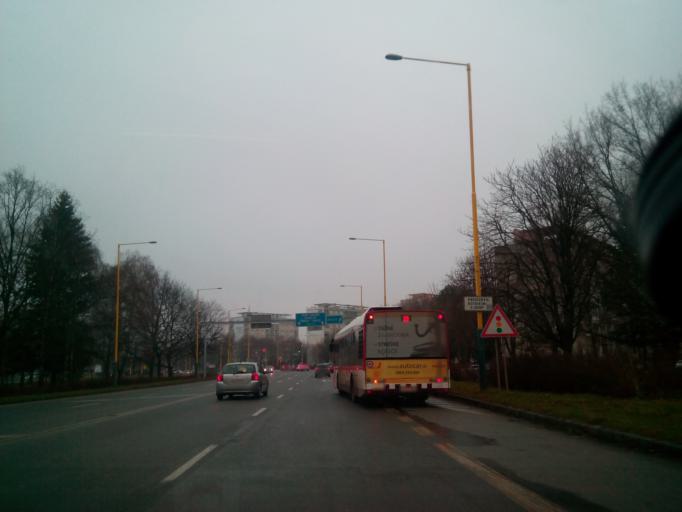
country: SK
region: Presovsky
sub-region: Okres Presov
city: Presov
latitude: 49.0005
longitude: 21.2242
